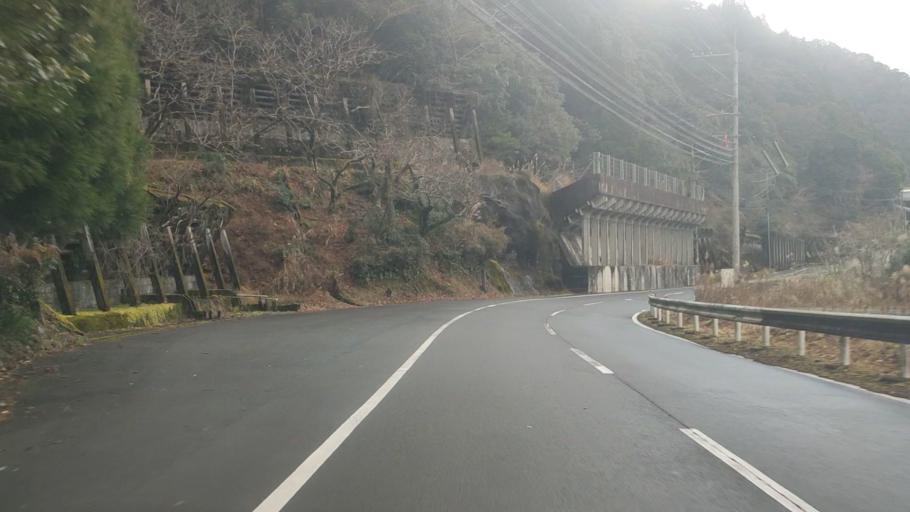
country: JP
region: Kumamoto
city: Hitoyoshi
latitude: 32.4289
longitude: 130.8584
